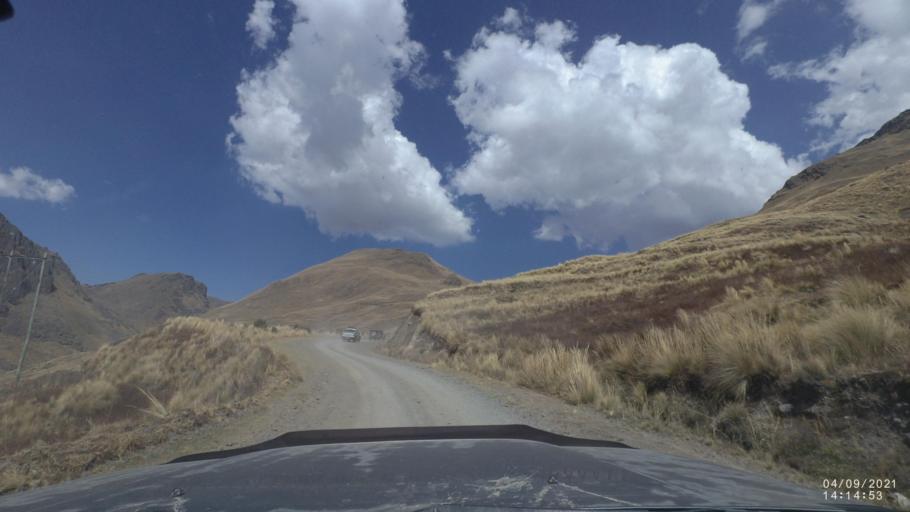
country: BO
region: Cochabamba
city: Sipe Sipe
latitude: -17.2274
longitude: -66.4428
